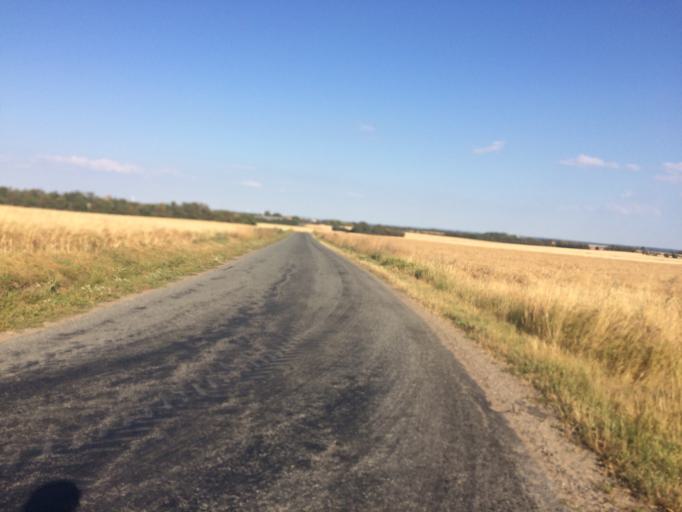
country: DK
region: Central Jutland
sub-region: Holstebro Kommune
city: Vinderup
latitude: 56.5884
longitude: 8.7629
